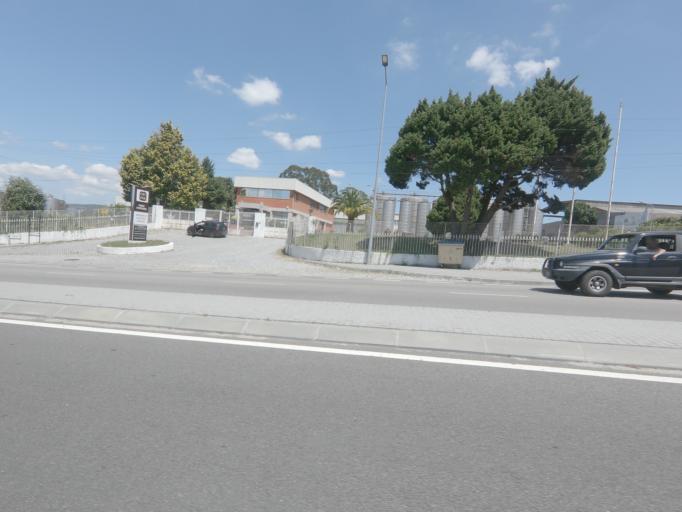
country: PT
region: Porto
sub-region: Paredes
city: Paredes
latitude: 41.1996
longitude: -8.3107
